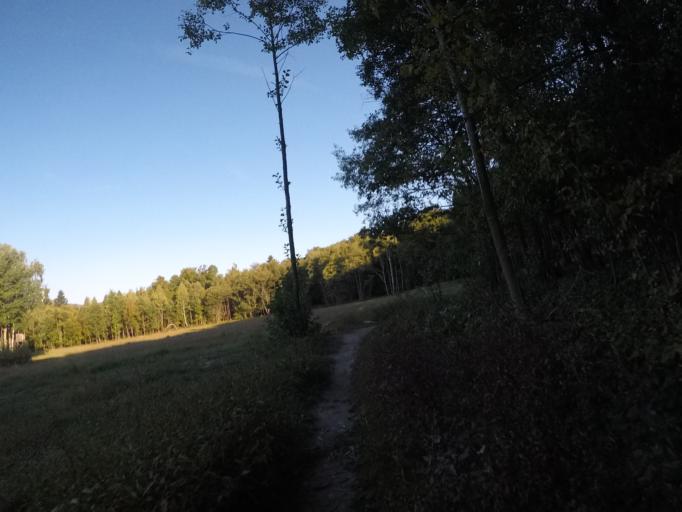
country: SK
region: Kosicky
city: Kosice
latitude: 48.7526
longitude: 21.1636
